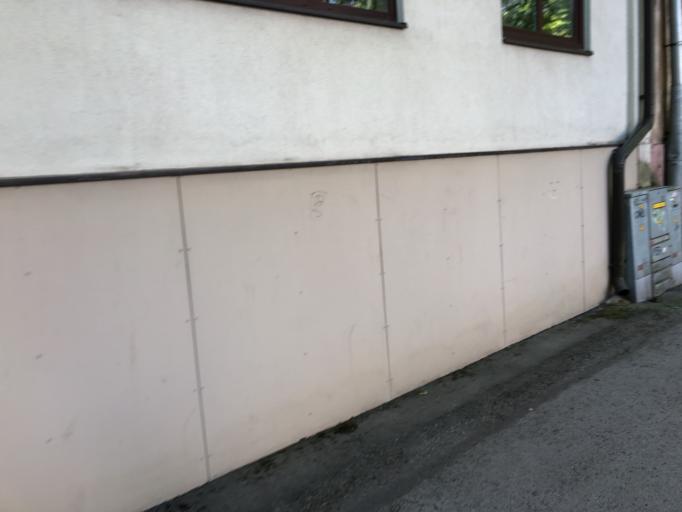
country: EE
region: Harju
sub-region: Tallinna linn
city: Tallinn
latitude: 59.4467
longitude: 24.7262
